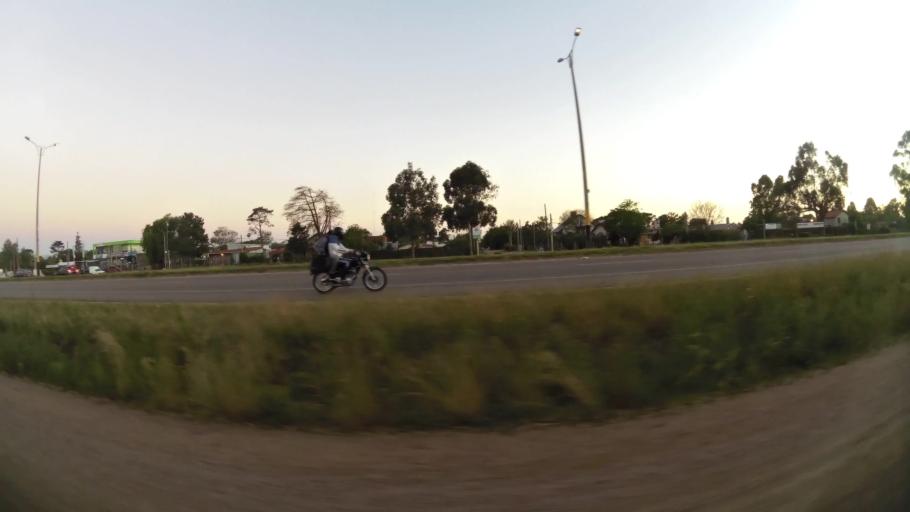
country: UY
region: Canelones
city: Colonia Nicolich
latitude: -34.8174
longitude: -55.9505
